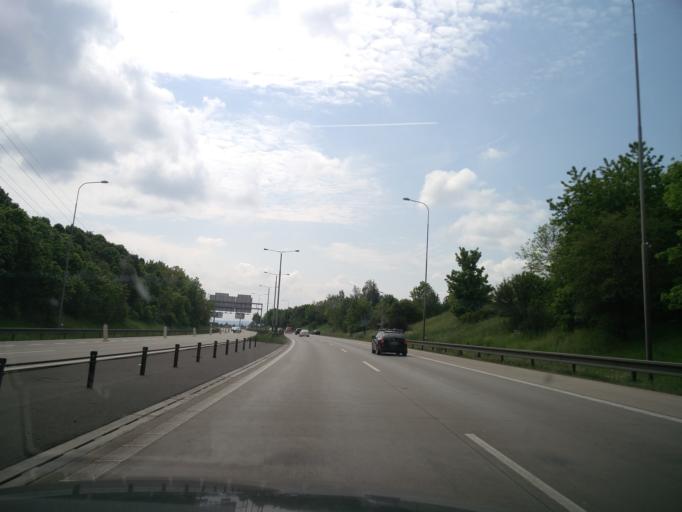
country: CZ
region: Central Bohemia
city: Rudna
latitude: 50.0434
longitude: 14.2702
